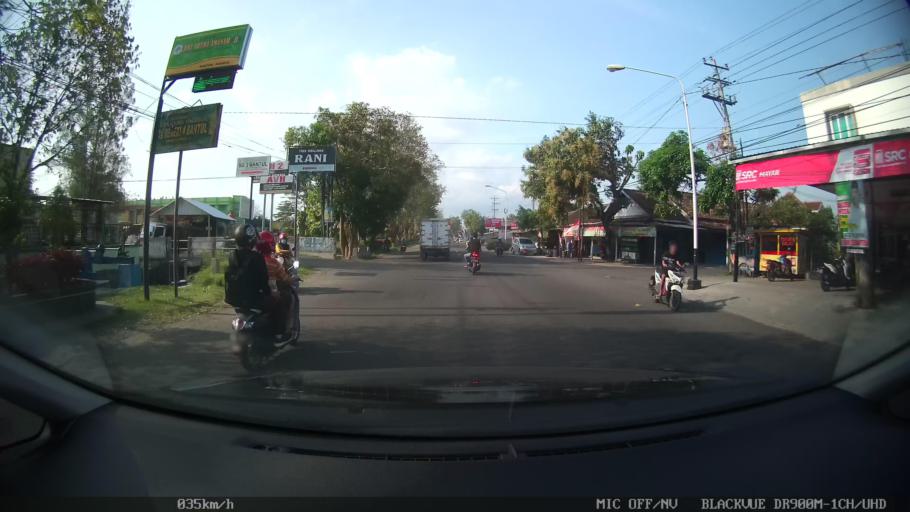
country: ID
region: Daerah Istimewa Yogyakarta
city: Bantul
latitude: -7.8969
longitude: 110.3233
